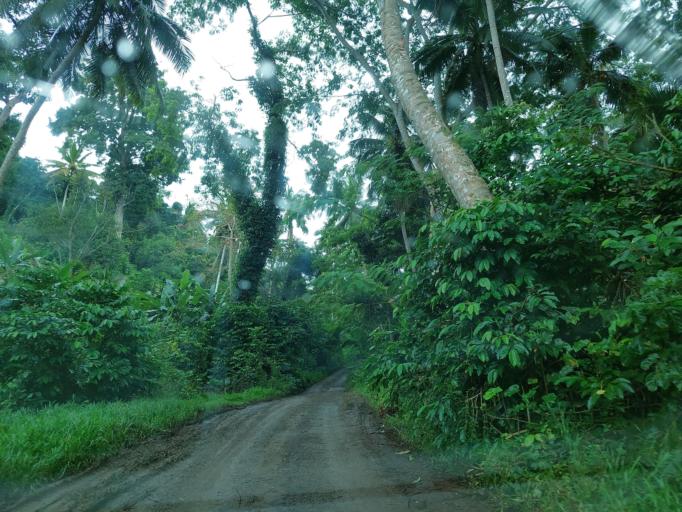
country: YT
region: Tsingoni
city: Tsingoni
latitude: -12.7663
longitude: 45.1223
